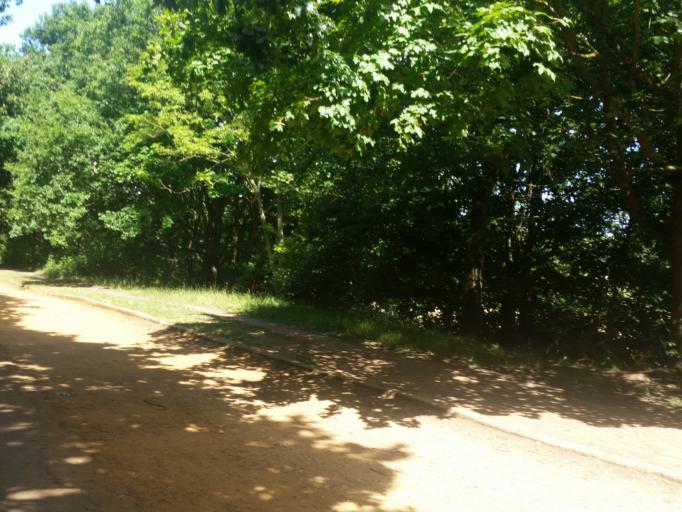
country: GB
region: England
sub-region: Greater London
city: Wood Green
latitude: 51.5935
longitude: -0.1248
